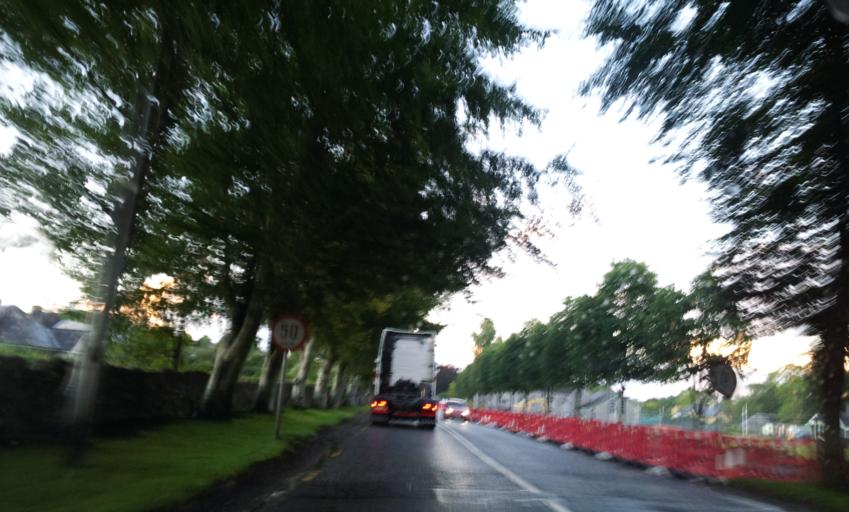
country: IE
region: Munster
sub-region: County Limerick
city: Adare
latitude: 52.5596
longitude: -8.7950
